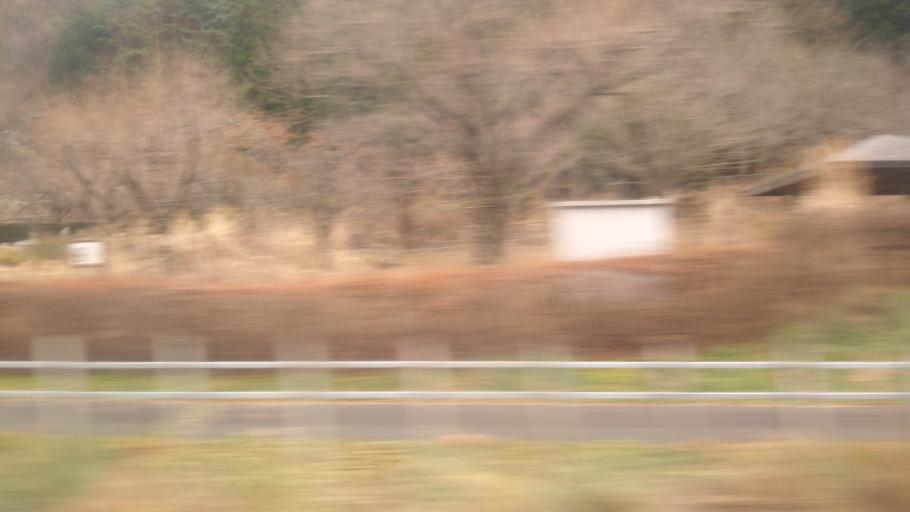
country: JP
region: Nagano
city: Shiojiri
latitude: 36.0507
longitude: 137.8960
